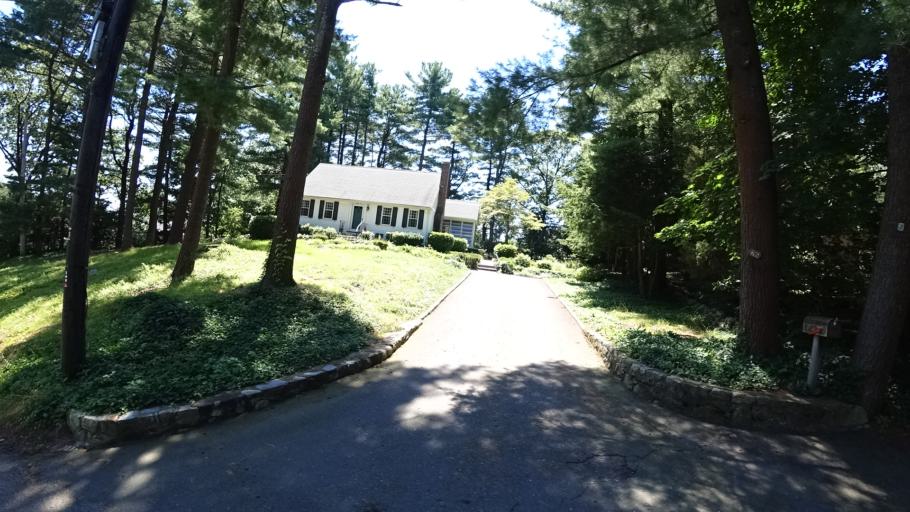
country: US
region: Massachusetts
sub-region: Norfolk County
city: Dedham
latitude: 42.2348
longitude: -71.1849
